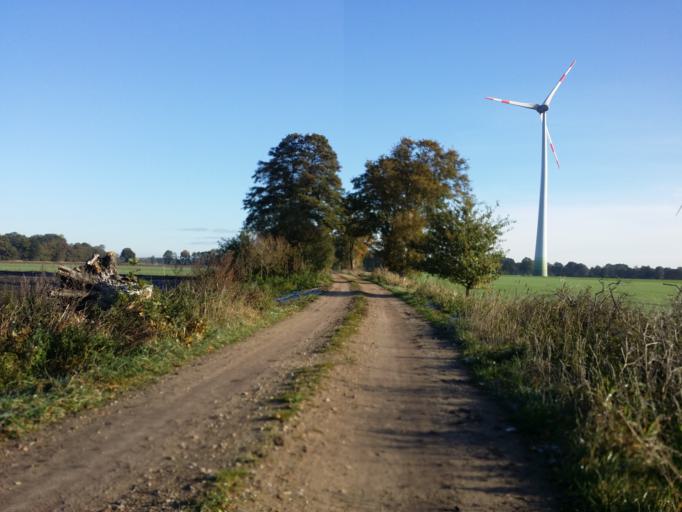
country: DE
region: Lower Saxony
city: Tarmstedt
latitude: 53.1962
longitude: 9.0500
